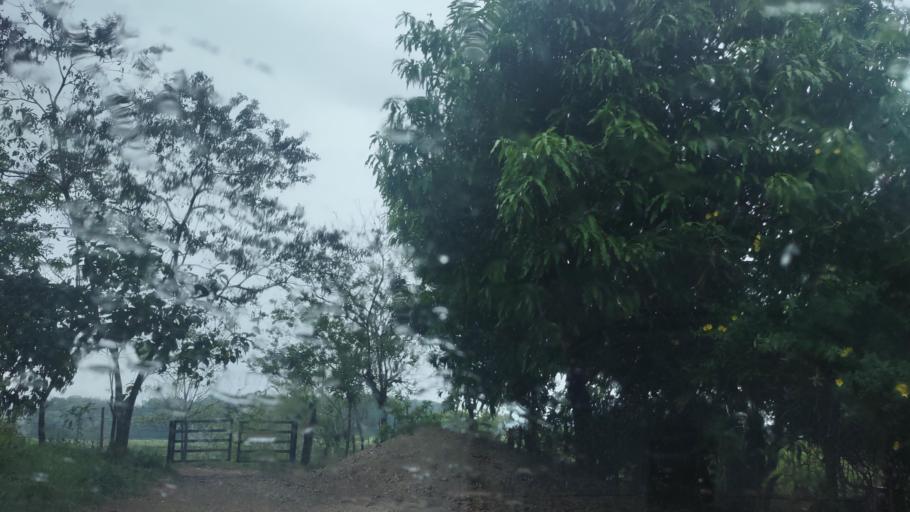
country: MX
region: Veracruz
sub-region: Uxpanapa
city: Poblado 10
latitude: 17.4474
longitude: -94.0988
